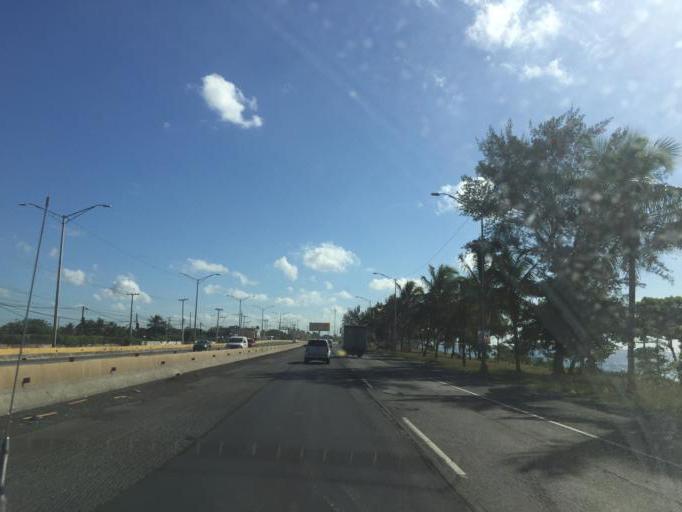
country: DO
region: Santo Domingo
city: Guerra
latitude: 18.4630
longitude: -69.7404
